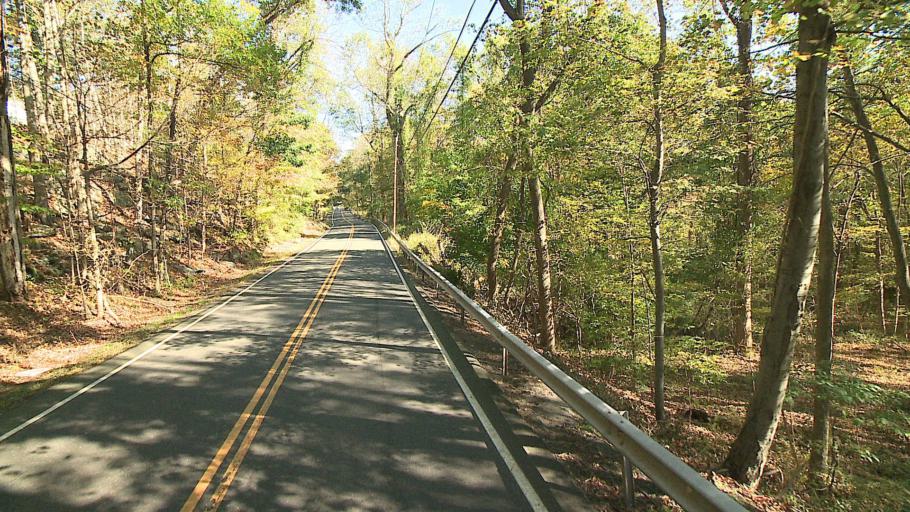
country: US
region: Connecticut
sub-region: Fairfield County
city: Trumbull
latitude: 41.2458
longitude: -73.3055
